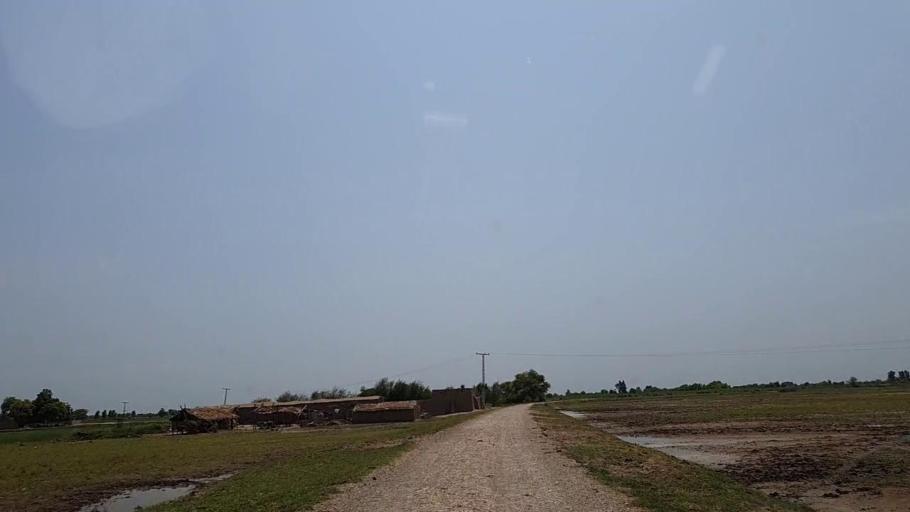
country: PK
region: Sindh
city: Ghotki
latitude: 27.9892
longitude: 69.4090
